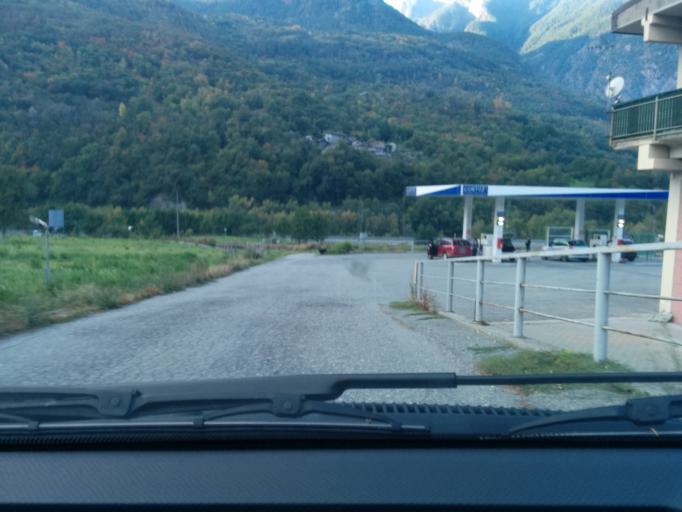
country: IT
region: Aosta Valley
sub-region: Valle d'Aosta
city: Nus
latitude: 45.7380
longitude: 7.4615
